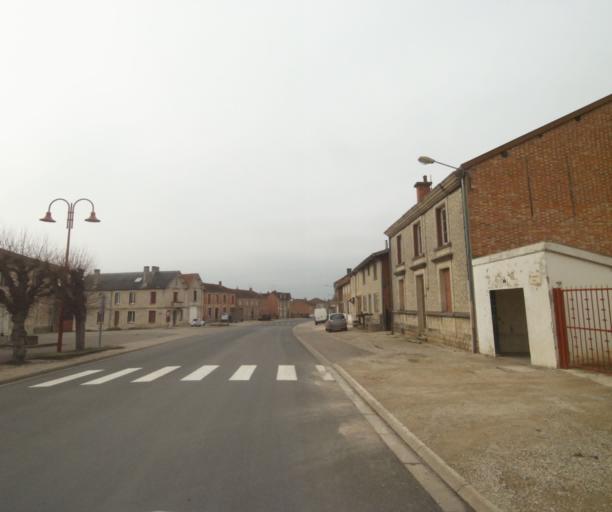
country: FR
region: Champagne-Ardenne
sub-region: Departement de la Marne
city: Pargny-sur-Saulx
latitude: 48.7494
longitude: 4.8499
